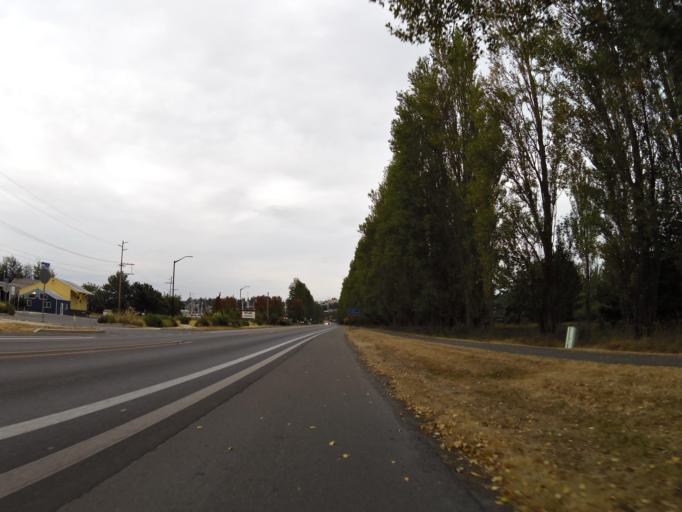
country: US
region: Washington
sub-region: Jefferson County
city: Port Townsend
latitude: 48.1096
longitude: -122.7727
